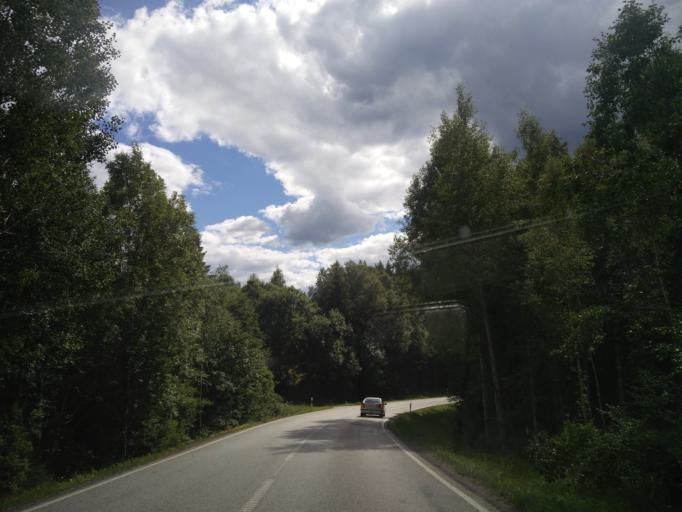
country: SE
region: OErebro
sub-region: Ljusnarsbergs Kommun
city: Kopparberg
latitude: 59.8445
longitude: 14.9990
